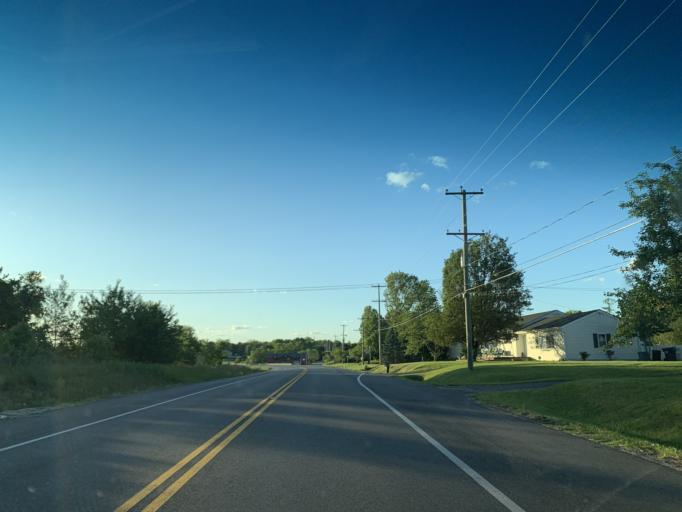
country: US
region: Maryland
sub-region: Cecil County
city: Elkton
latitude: 39.6524
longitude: -75.8500
